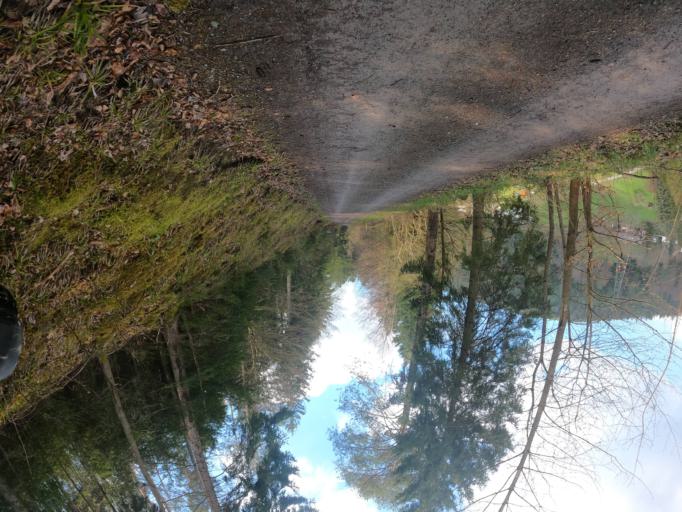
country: DE
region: Baden-Wuerttemberg
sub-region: Karlsruhe Region
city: Hofen an der Enz
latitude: 48.7742
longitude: 8.5932
